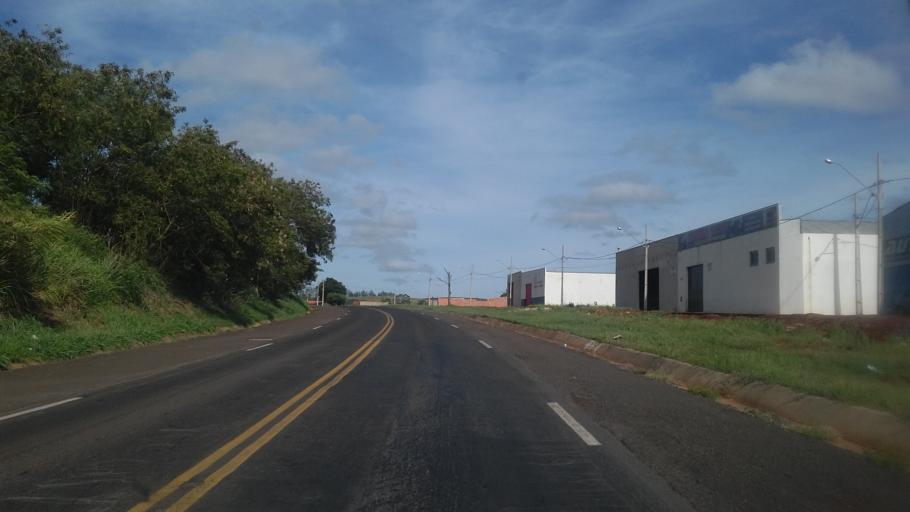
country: BR
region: Parana
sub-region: Santo Antonio Da Platina
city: Santo Antonio da Platina
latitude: -23.2770
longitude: -50.0639
